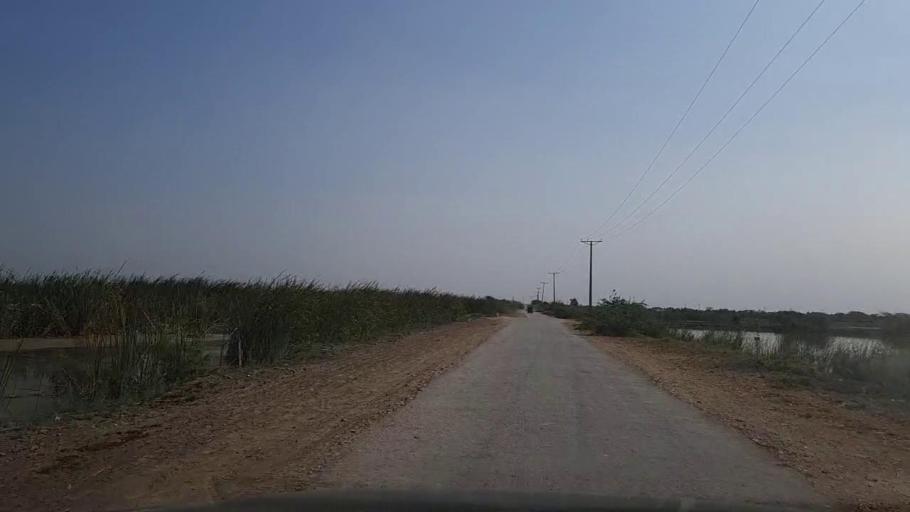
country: PK
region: Sindh
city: Thatta
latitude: 24.5838
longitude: 67.9099
